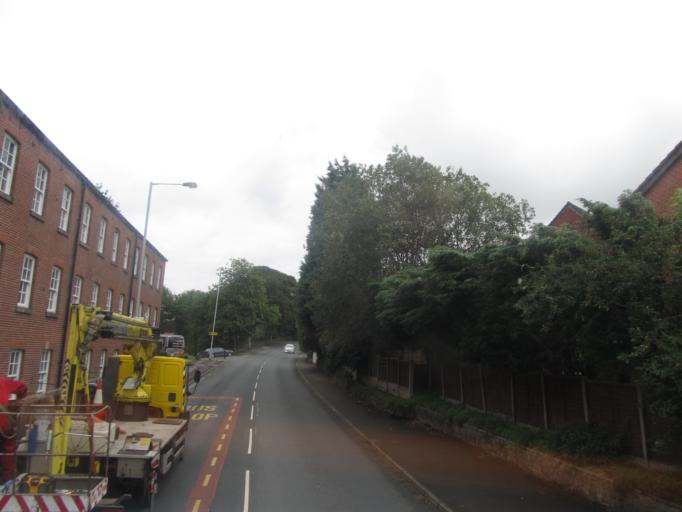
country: GB
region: England
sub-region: Borough of Tameside
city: Haughton Green
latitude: 53.4284
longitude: -2.0950
